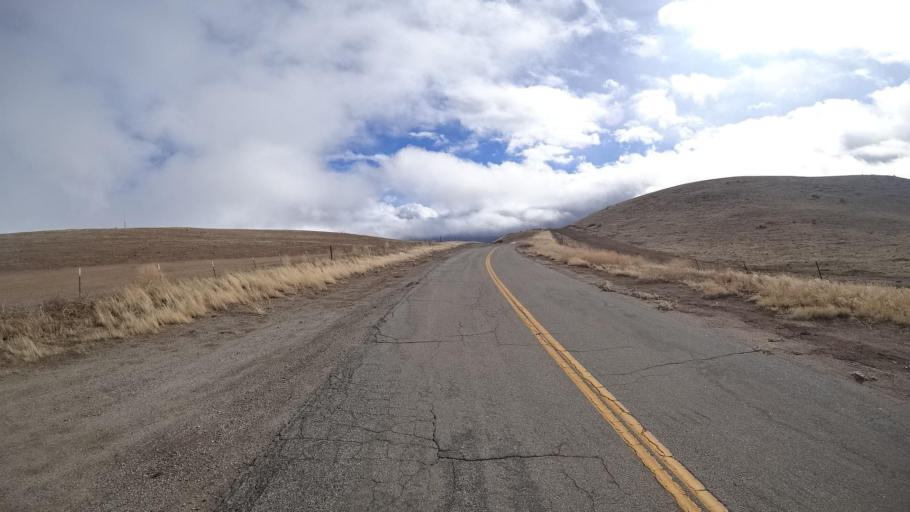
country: US
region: California
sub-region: Kern County
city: Maricopa
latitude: 34.9025
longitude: -119.3710
